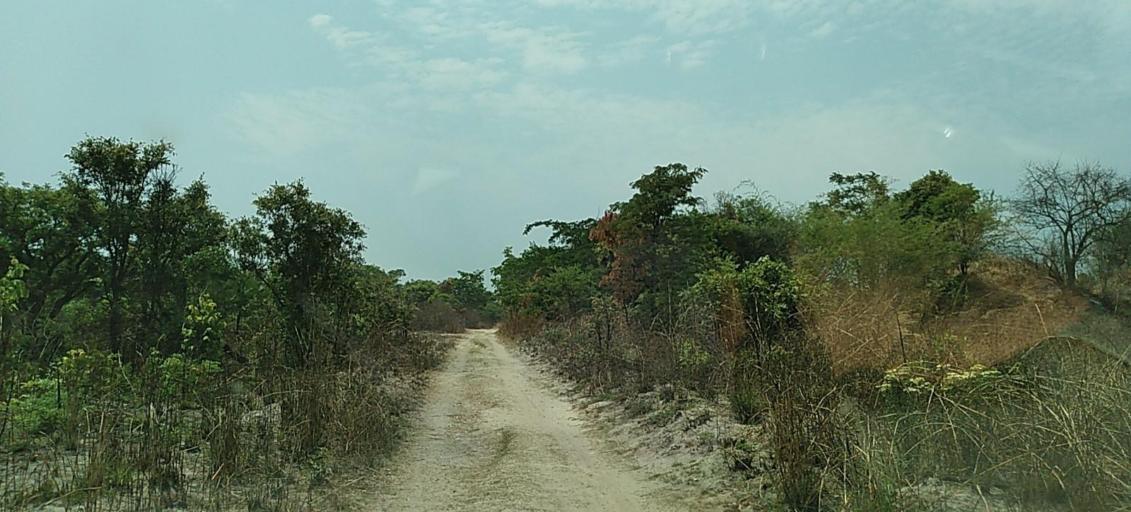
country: ZM
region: Copperbelt
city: Kalulushi
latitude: -12.9509
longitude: 28.1358
